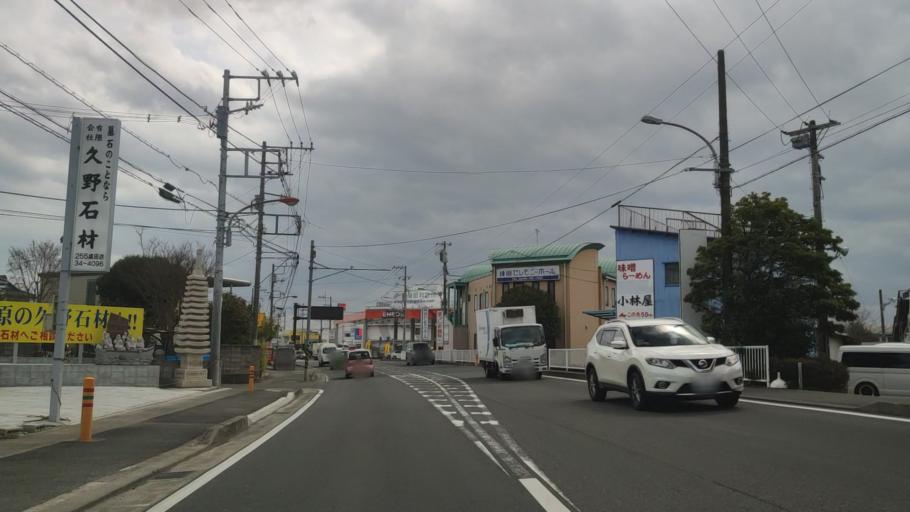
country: JP
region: Kanagawa
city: Odawara
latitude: 35.2893
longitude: 139.1679
